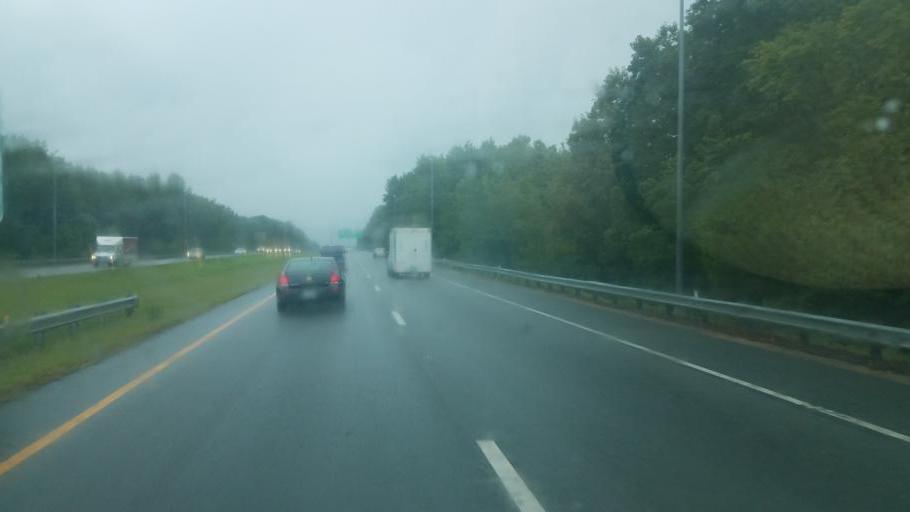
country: US
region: Virginia
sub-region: City of Portsmouth
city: Portsmouth Heights
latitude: 36.7596
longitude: -76.3294
